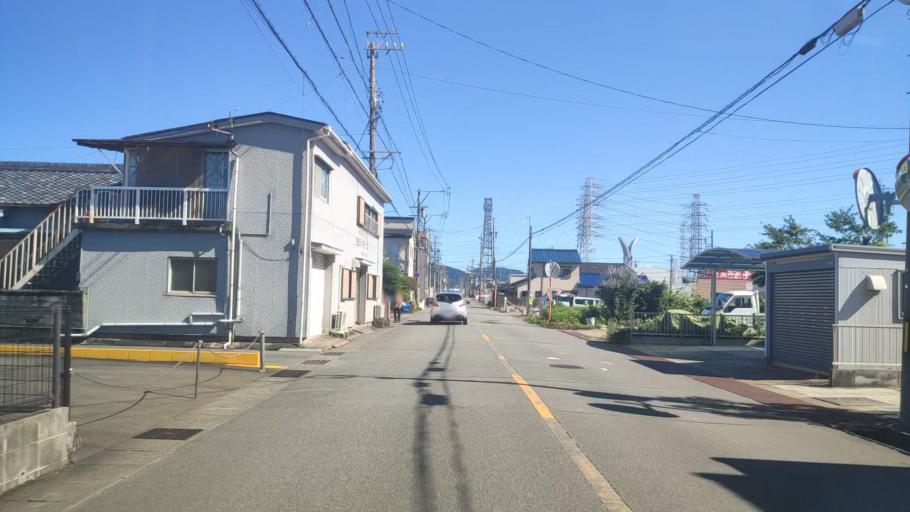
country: JP
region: Mie
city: Ise
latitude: 34.5105
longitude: 136.7165
